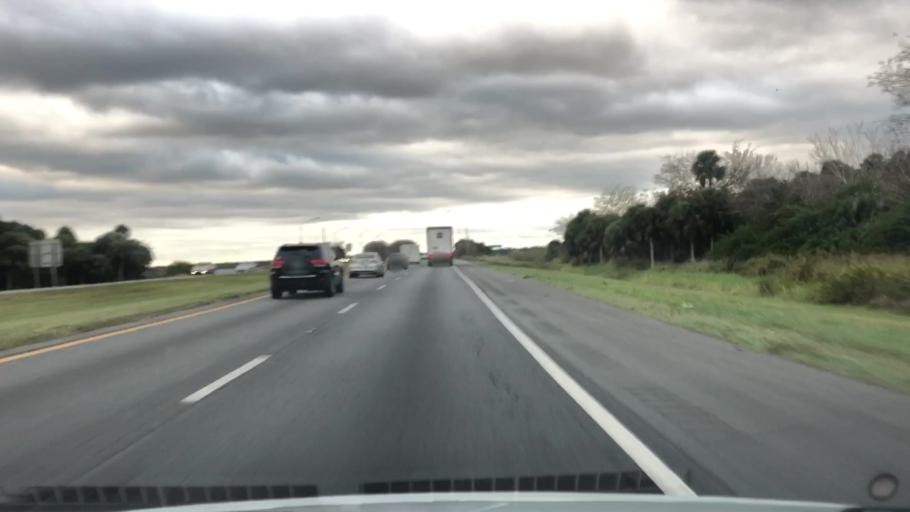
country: US
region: Florida
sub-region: Seminole County
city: Oviedo
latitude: 28.7234
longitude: -81.2461
